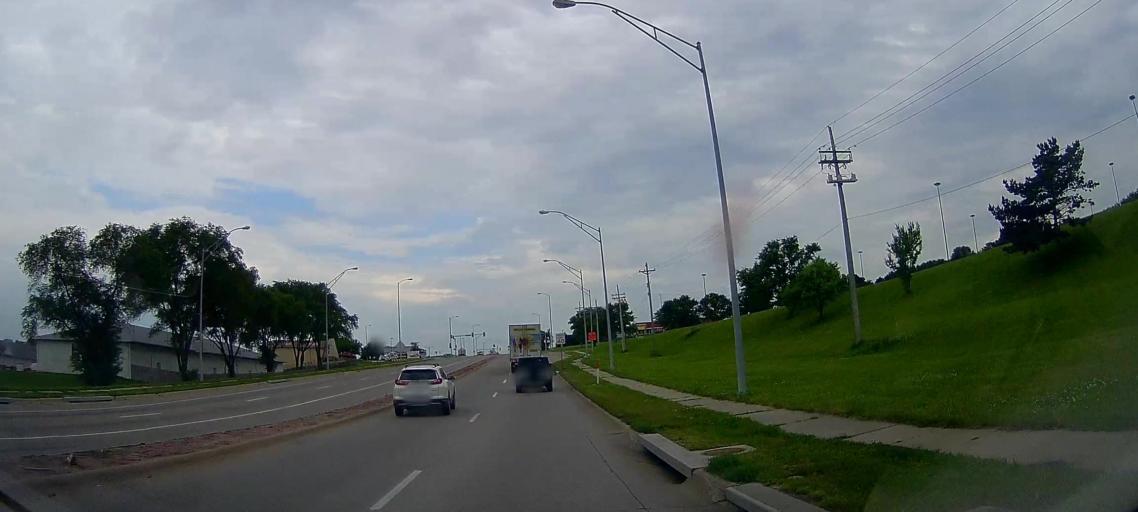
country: US
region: Nebraska
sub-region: Douglas County
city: Ralston
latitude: 41.3127
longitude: -96.0528
